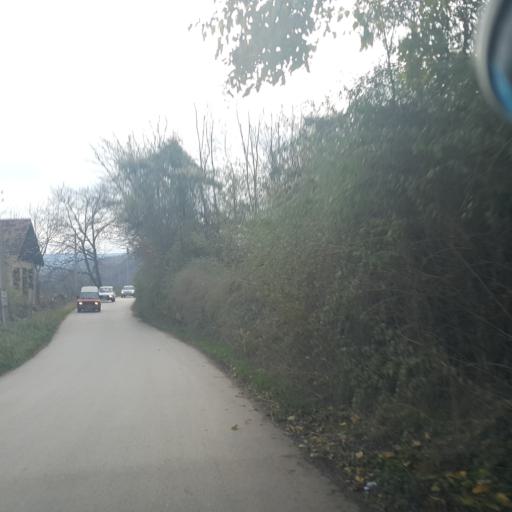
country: RS
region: Central Serbia
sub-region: Zajecarski Okrug
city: Knjazevac
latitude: 43.5888
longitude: 22.2510
